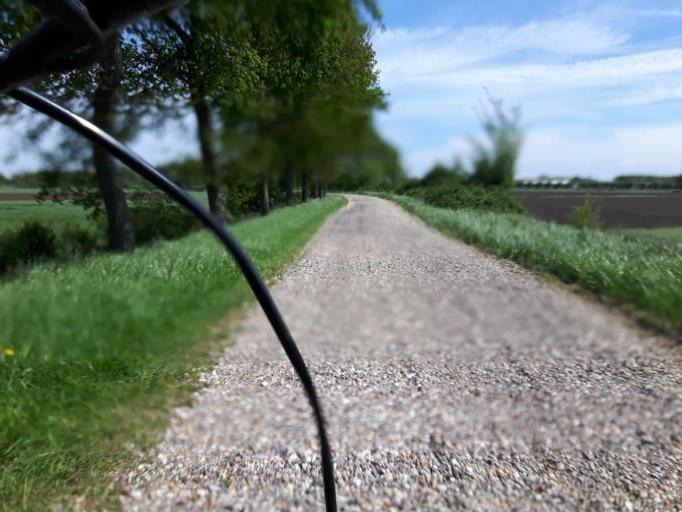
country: NL
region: Zeeland
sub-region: Gemeente Goes
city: Goes
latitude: 51.4430
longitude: 3.8502
